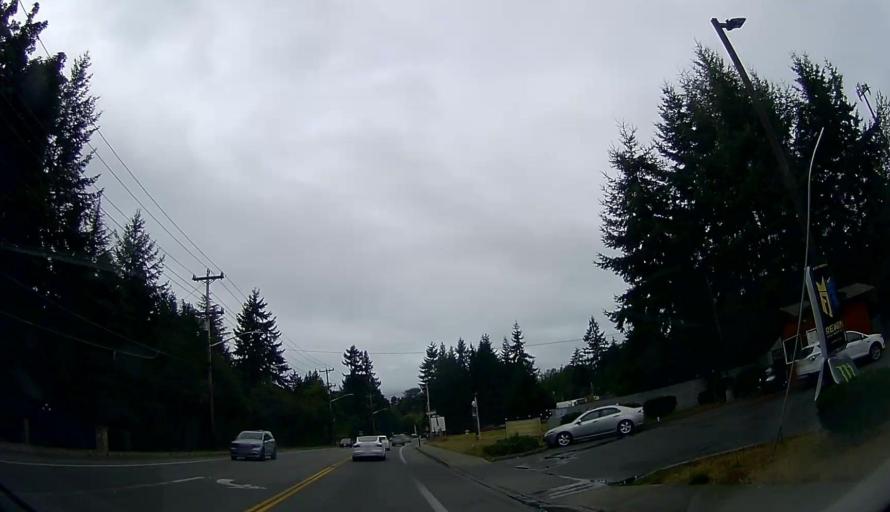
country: US
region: Washington
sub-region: Snohomish County
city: Marysville
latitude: 48.0392
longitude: -122.2295
